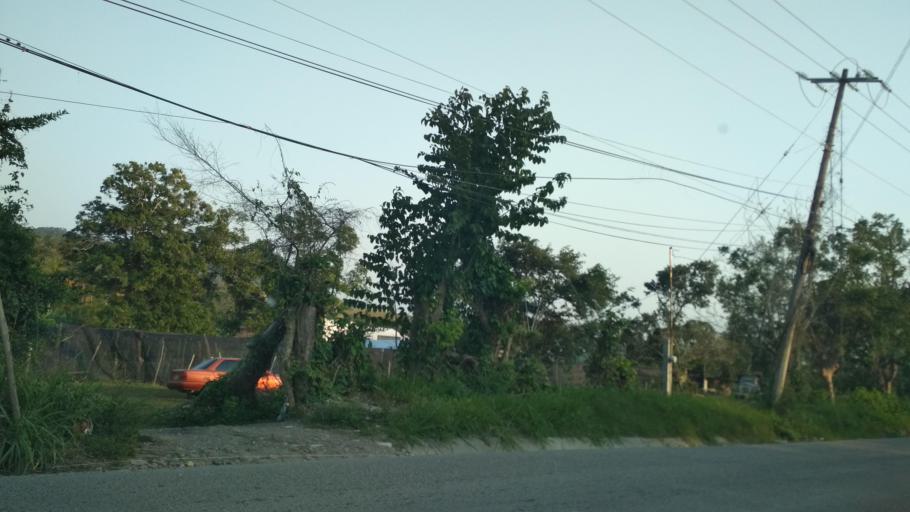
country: MM
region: Shan
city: Taunggyi
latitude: 20.4125
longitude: 97.3365
